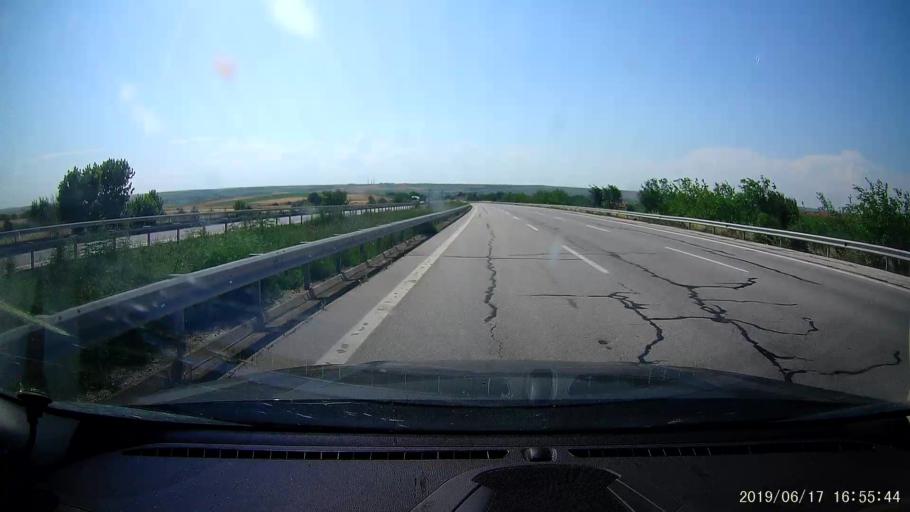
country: TR
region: Edirne
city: Haskoy
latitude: 41.5808
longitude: 26.9574
